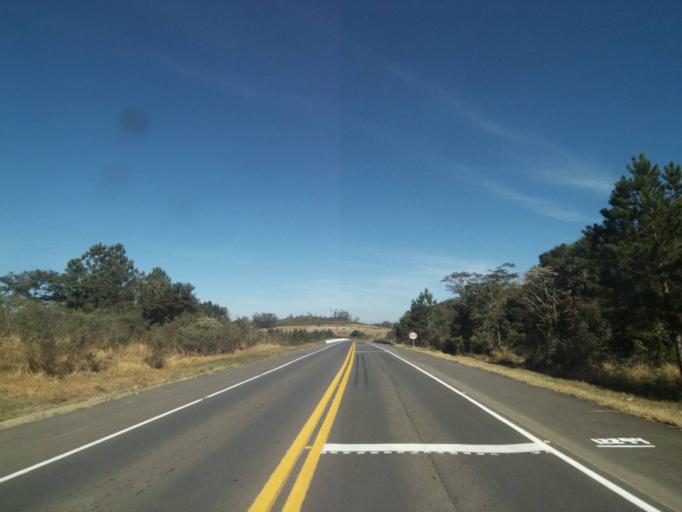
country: BR
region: Parana
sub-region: Tibagi
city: Tibagi
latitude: -24.8114
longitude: -50.4829
